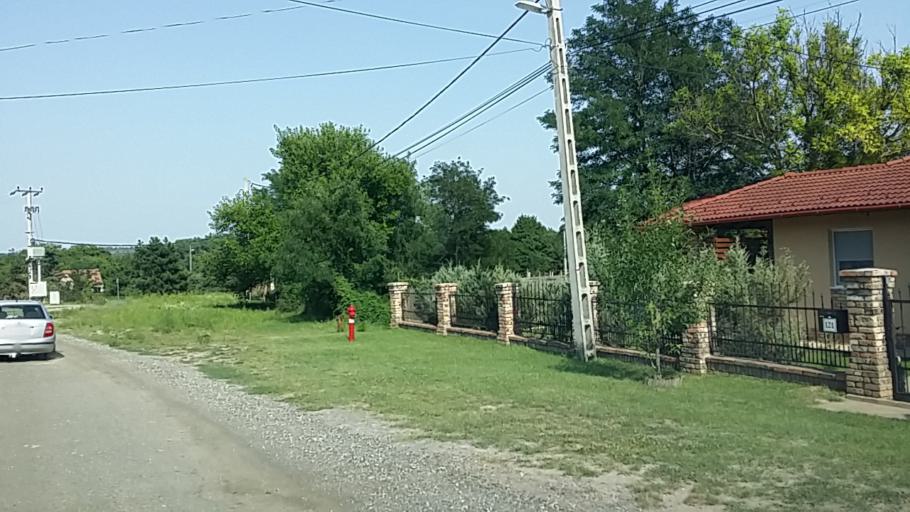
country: HU
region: Pest
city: Erdokertes
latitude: 47.6655
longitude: 19.3356
